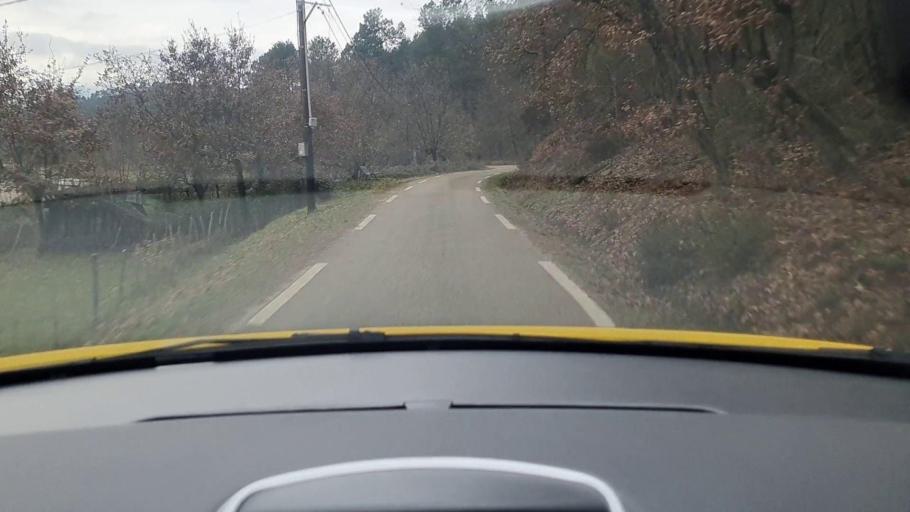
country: FR
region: Languedoc-Roussillon
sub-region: Departement du Gard
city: Besseges
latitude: 44.3258
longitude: 4.1194
